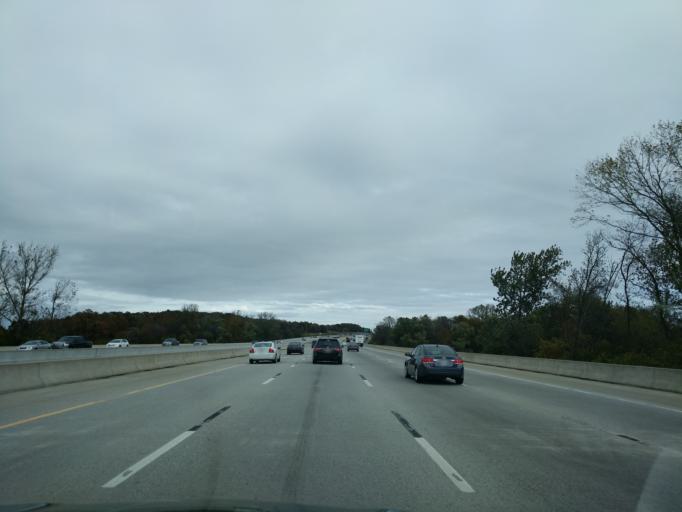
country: US
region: North Carolina
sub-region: Rowan County
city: Spencer
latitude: 35.7174
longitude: -80.3910
